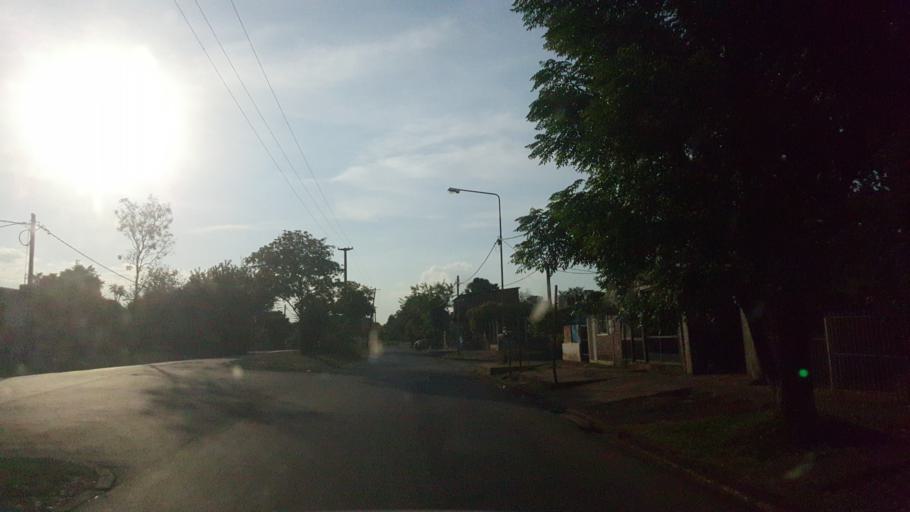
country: AR
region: Misiones
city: Garupa
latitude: -27.4340
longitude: -55.8750
